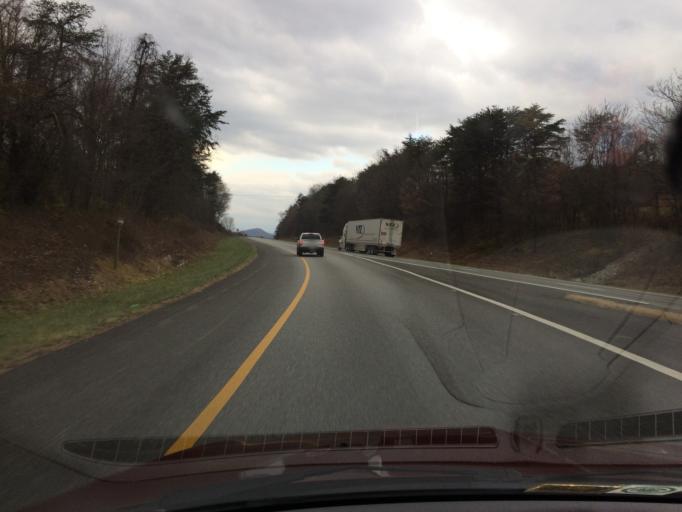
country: US
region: Virginia
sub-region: Roanoke County
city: Hollins
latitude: 37.3408
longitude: -79.9996
